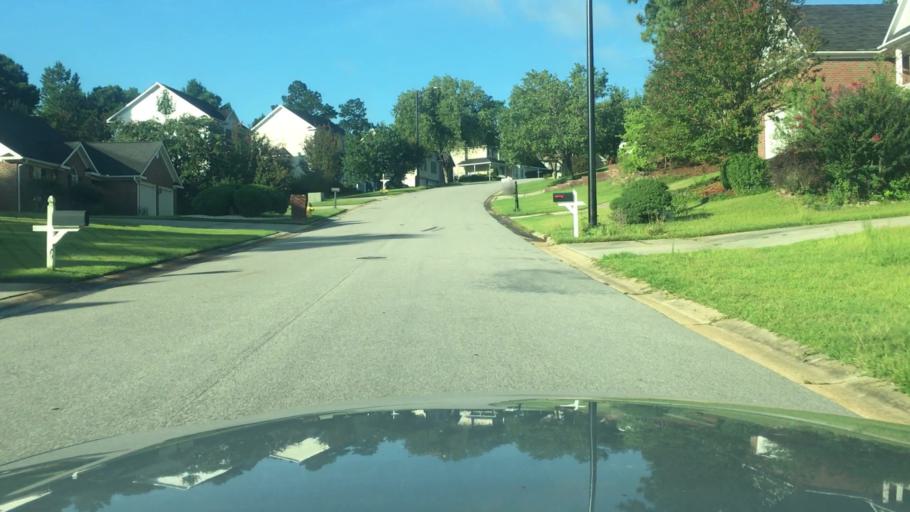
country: US
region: North Carolina
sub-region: Cumberland County
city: Fayetteville
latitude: 35.1410
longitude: -78.8842
